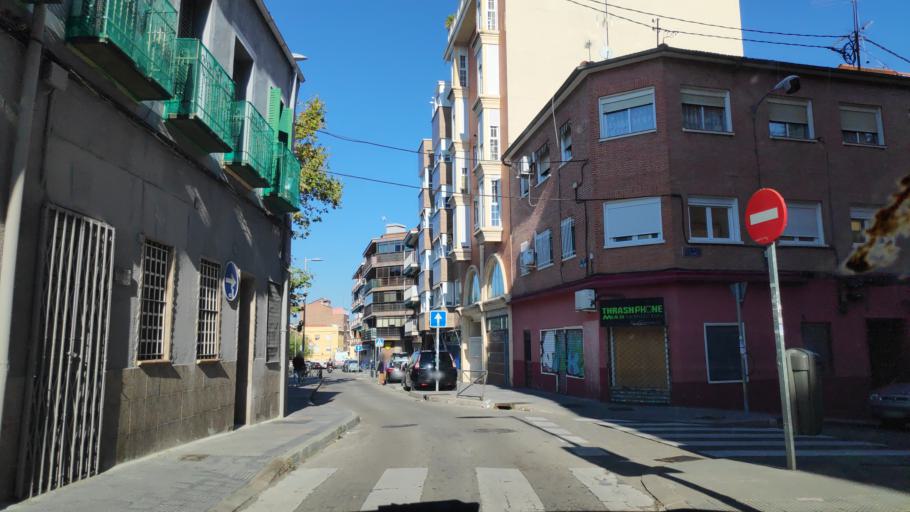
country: ES
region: Madrid
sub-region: Provincia de Madrid
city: Tetuan de las Victorias
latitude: 40.4677
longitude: -3.6976
